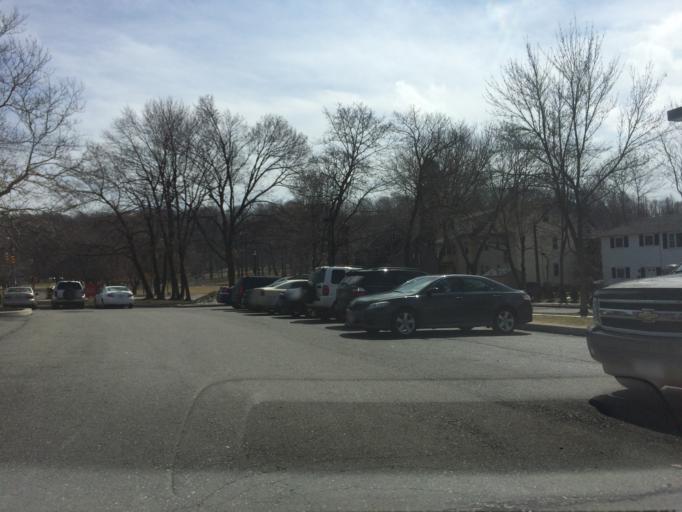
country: US
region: New York
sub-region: Monroe County
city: Brighton
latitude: 43.1418
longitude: -77.5773
